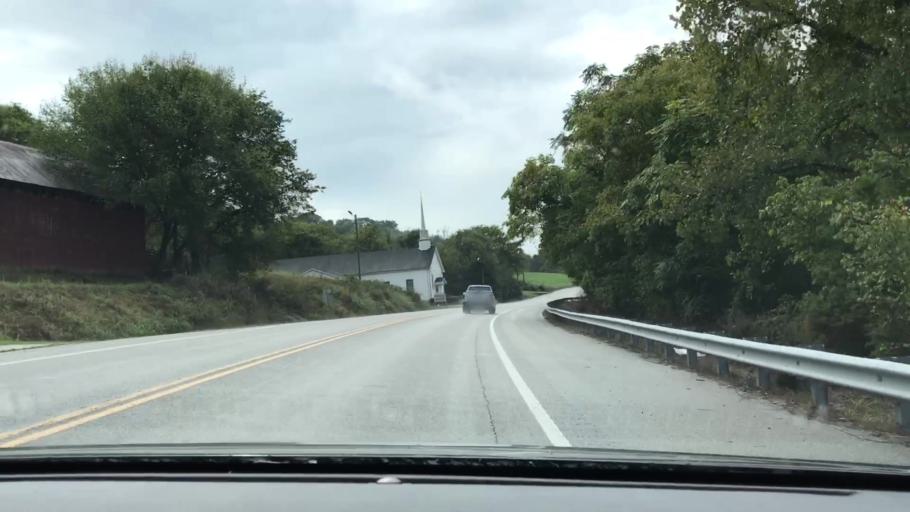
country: US
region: Tennessee
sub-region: Smith County
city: Carthage
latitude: 36.3046
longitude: -85.9750
